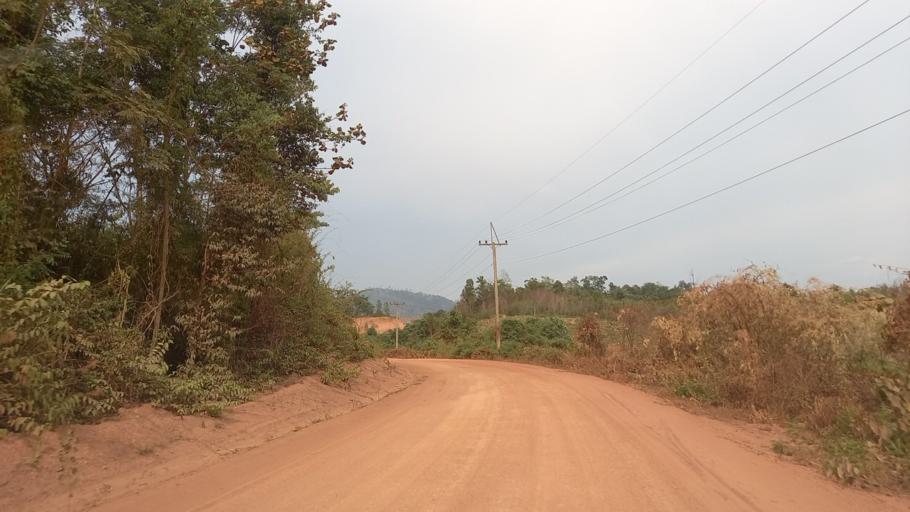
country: LA
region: Bolikhamxai
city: Bolikhan
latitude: 18.5365
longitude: 103.8048
